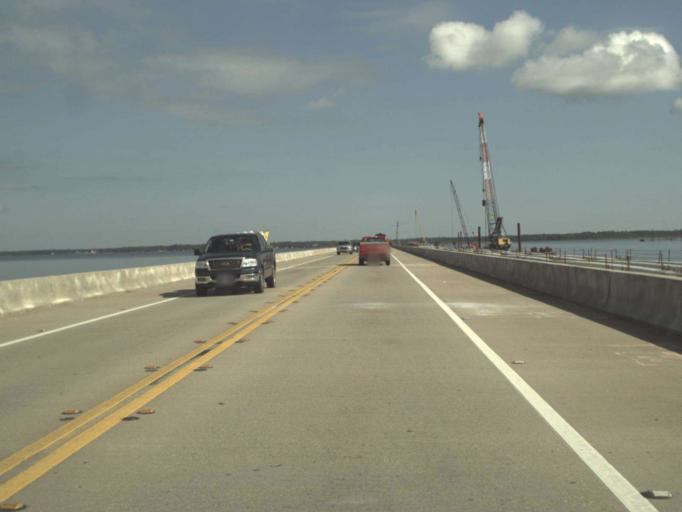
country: US
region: Florida
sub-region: Walton County
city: Seaside
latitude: 30.4062
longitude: -86.1660
